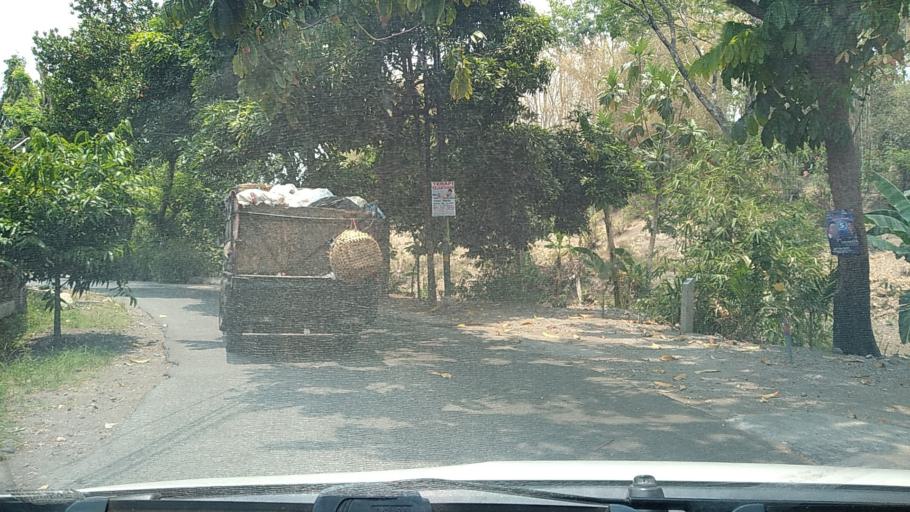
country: ID
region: Central Java
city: Semarang
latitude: -7.0013
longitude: 110.3669
